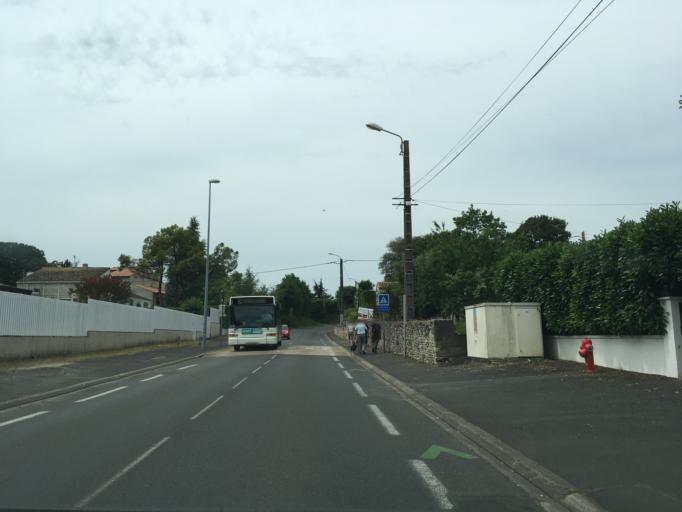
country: FR
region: Poitou-Charentes
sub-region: Departement des Deux-Sevres
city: Bessines
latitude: 46.3188
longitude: -0.5076
